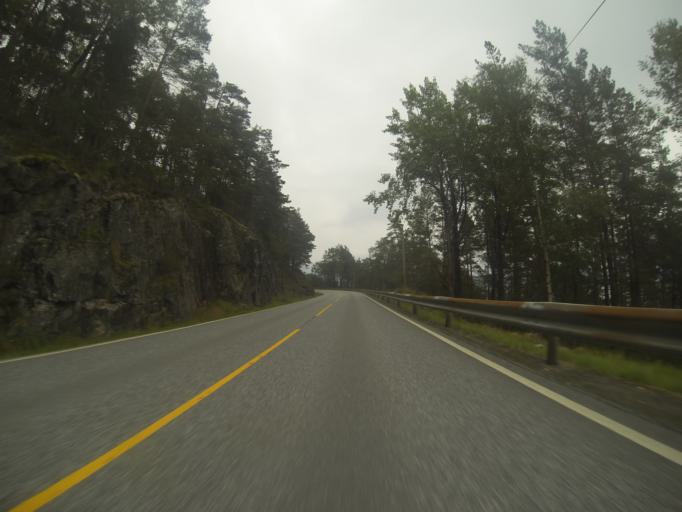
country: NO
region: Rogaland
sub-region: Suldal
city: Sand
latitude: 59.5203
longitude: 6.2431
